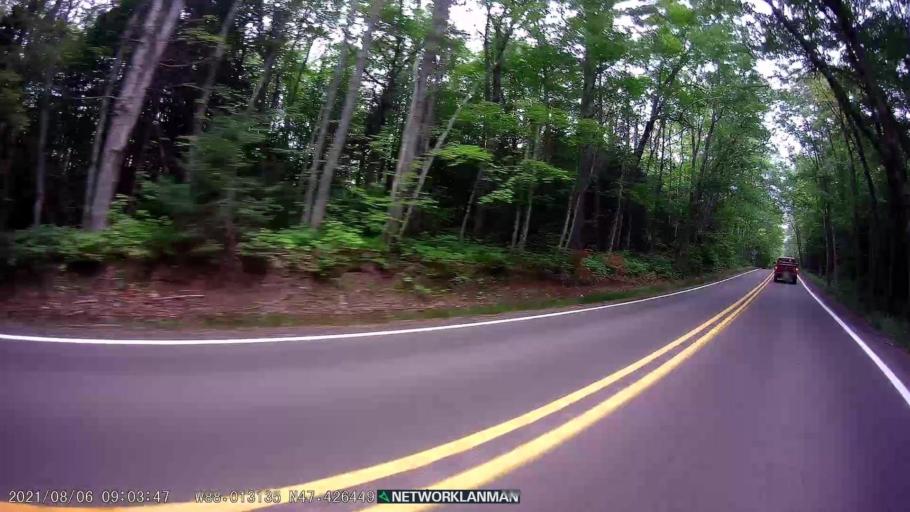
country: US
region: Michigan
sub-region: Keweenaw County
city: Eagle River
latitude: 47.4266
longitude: -88.0127
